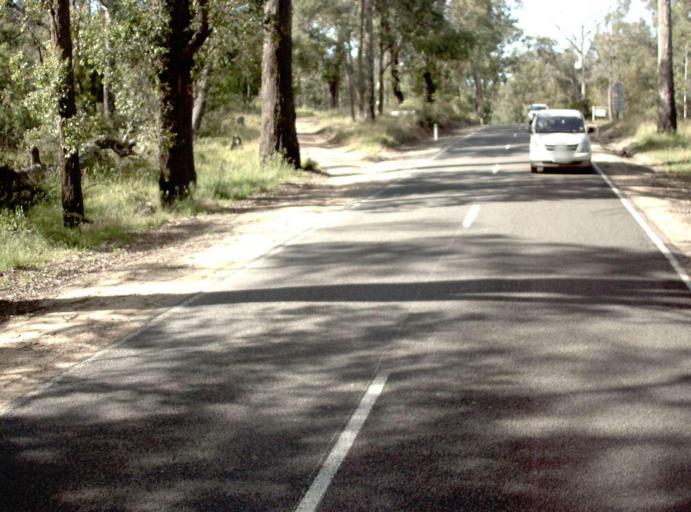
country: AU
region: Victoria
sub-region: East Gippsland
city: Lakes Entrance
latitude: -37.5437
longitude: 148.1484
